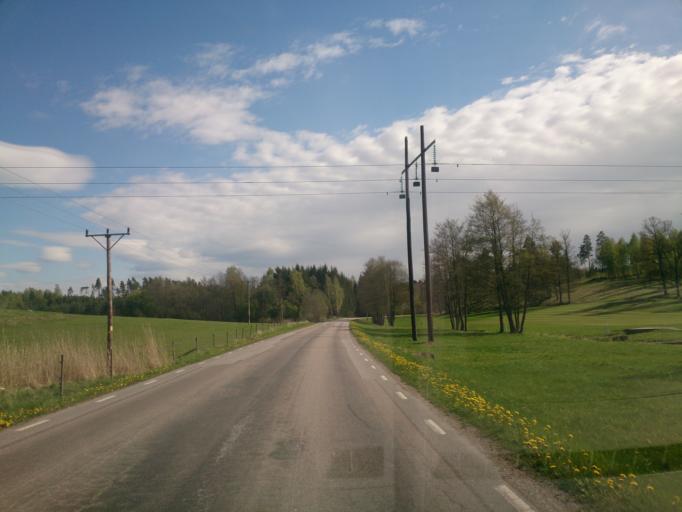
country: SE
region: OEstergoetland
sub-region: Linkopings Kommun
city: Ljungsbro
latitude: 58.5245
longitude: 15.5233
